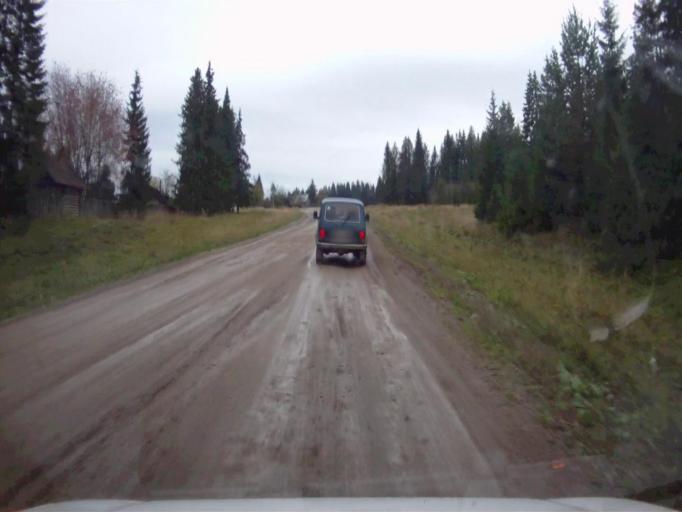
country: RU
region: Chelyabinsk
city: Nyazepetrovsk
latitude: 56.0627
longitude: 59.5655
